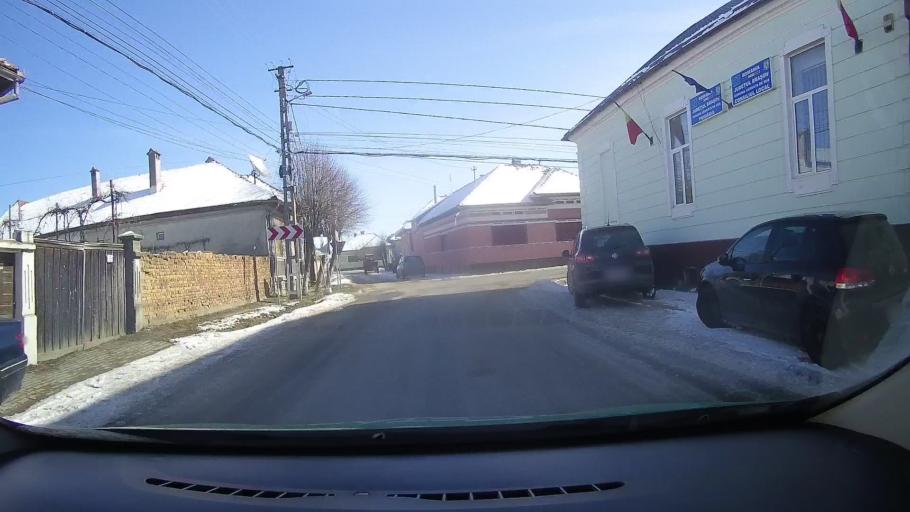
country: RO
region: Brasov
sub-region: Comuna Sambata de Sus
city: Sambata de Sus
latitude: 45.7604
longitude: 24.8300
